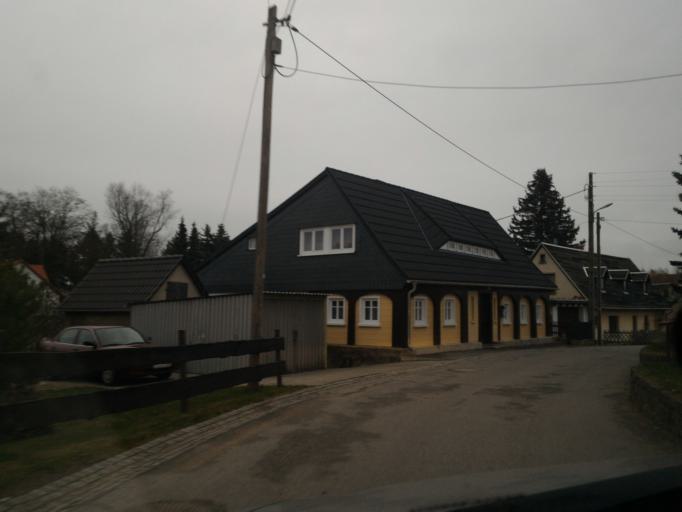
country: DE
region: Saxony
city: Leutersdorf
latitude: 50.9636
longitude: 14.6479
